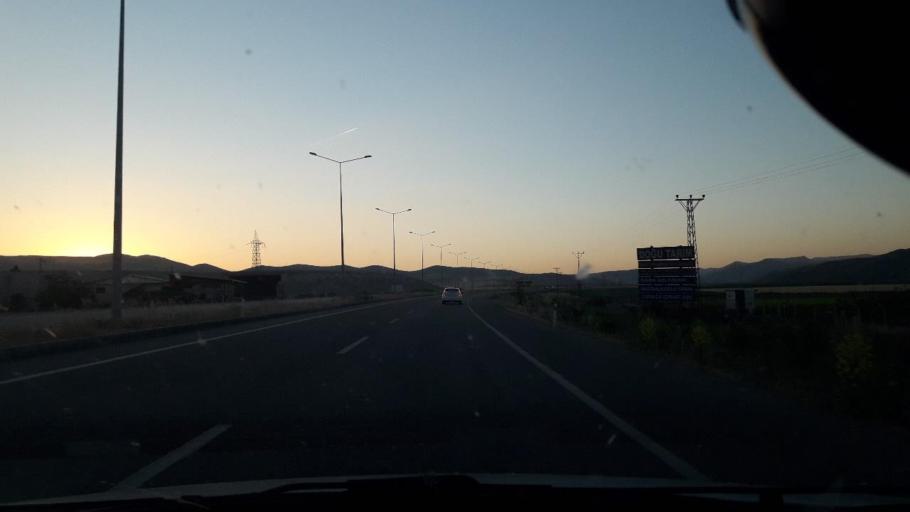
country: TR
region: Malatya
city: Yazihan
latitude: 38.6011
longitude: 38.1817
